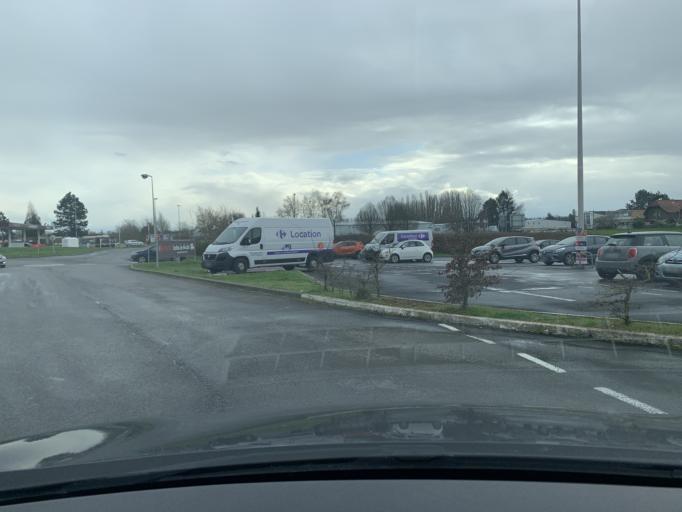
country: FR
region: Nord-Pas-de-Calais
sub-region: Departement du Nord
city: Proville
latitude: 50.1776
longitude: 3.2053
